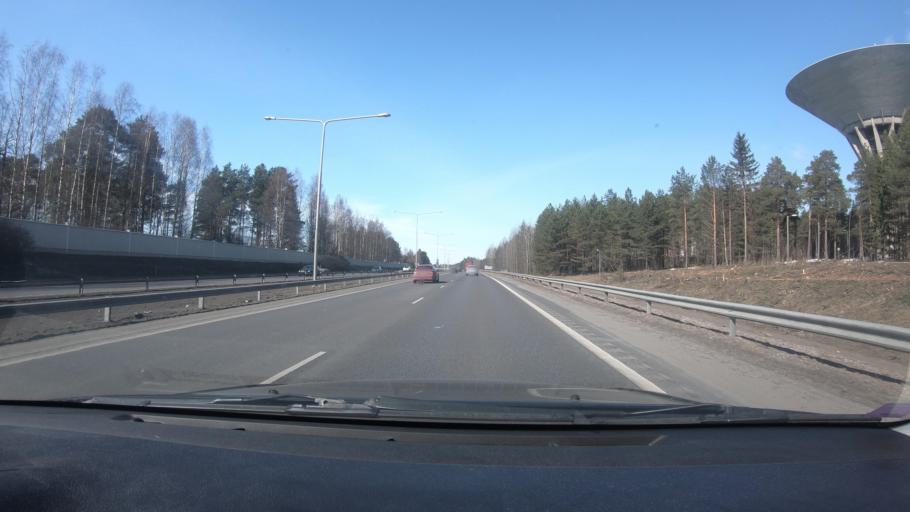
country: FI
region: Northern Ostrobothnia
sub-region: Oulu
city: Oulu
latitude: 65.0361
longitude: 25.4860
